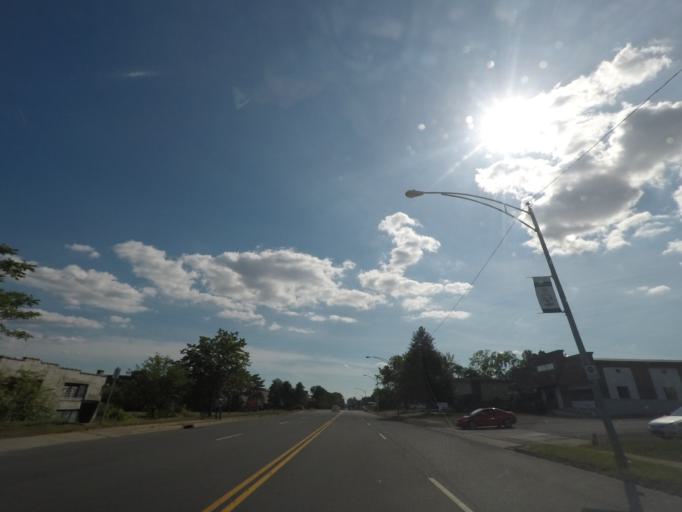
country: US
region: New York
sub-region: Albany County
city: Menands
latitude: 42.6798
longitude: -73.7333
